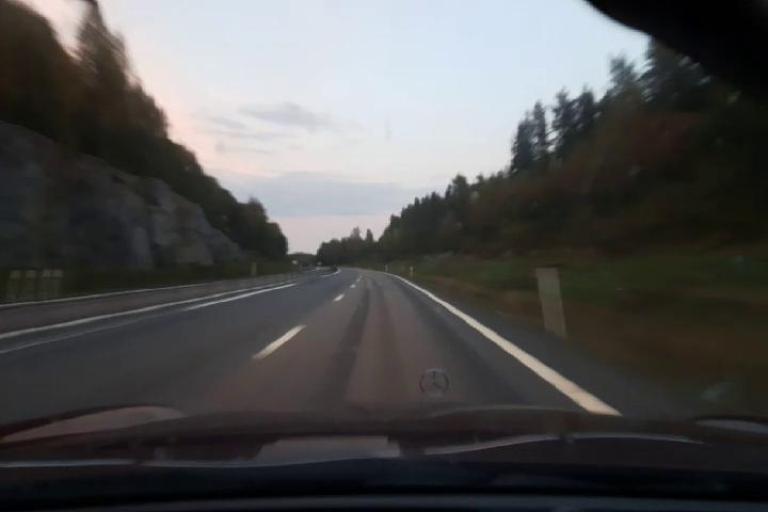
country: SE
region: Vaesternorrland
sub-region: Haernoesands Kommun
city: Haernoesand
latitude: 62.8660
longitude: 18.0370
